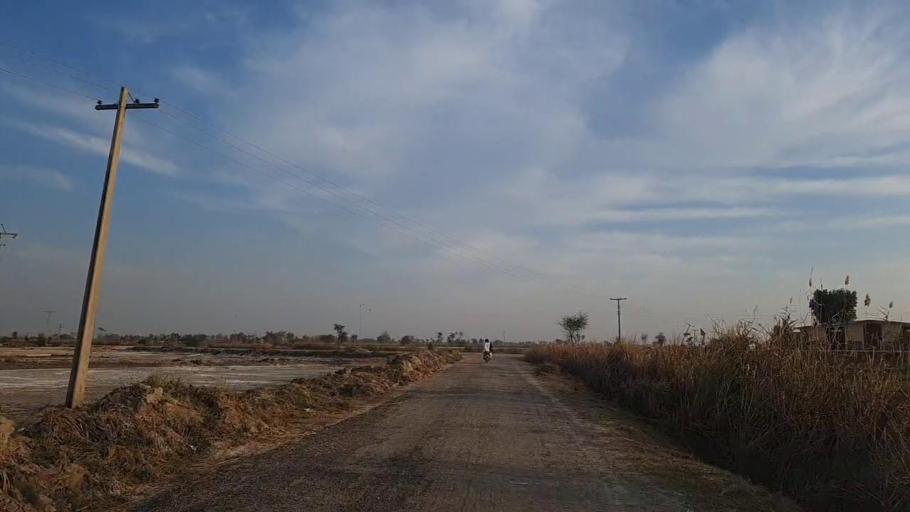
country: PK
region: Sindh
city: Bandhi
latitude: 26.5751
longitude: 68.3374
